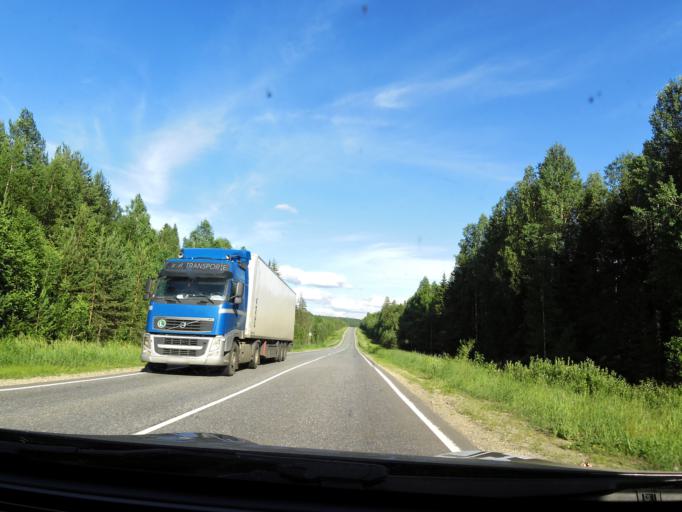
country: RU
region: Kirov
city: Chernaya Kholunitsa
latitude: 58.8263
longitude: 51.7815
